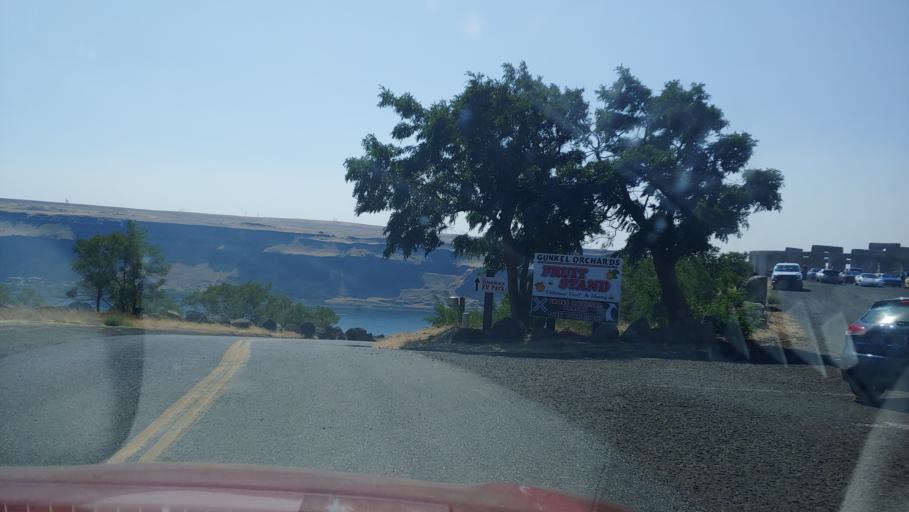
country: US
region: Washington
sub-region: Klickitat County
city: Goldendale
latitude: 45.6957
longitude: -120.8054
